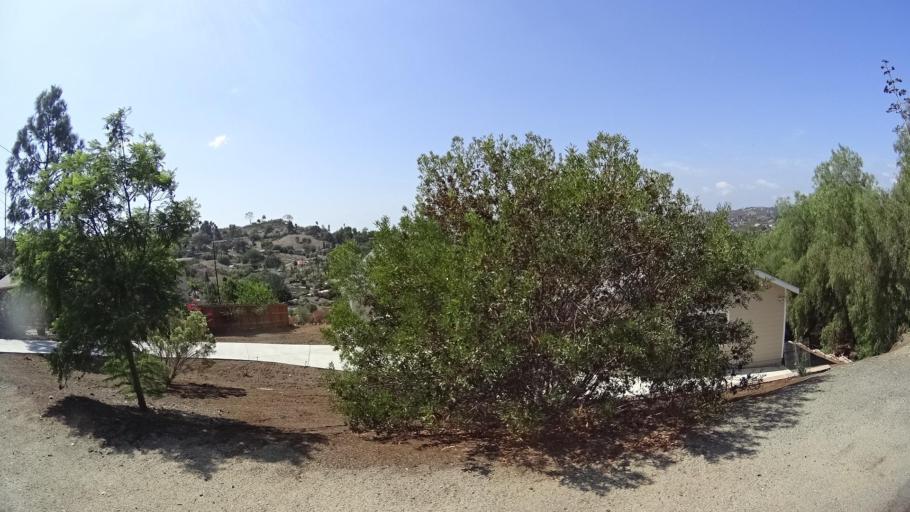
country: US
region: California
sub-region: San Diego County
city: Spring Valley
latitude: 32.7418
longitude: -116.9849
